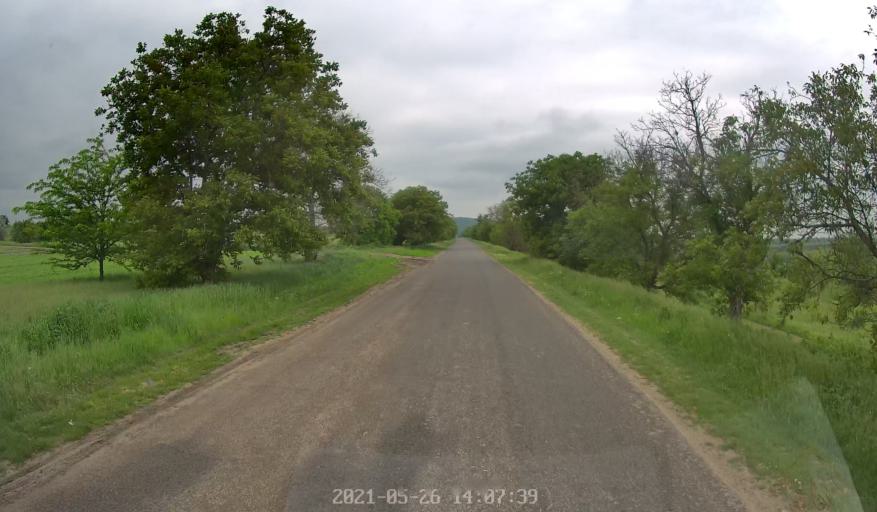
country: MD
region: Hincesti
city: Dancu
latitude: 46.7451
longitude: 28.3564
